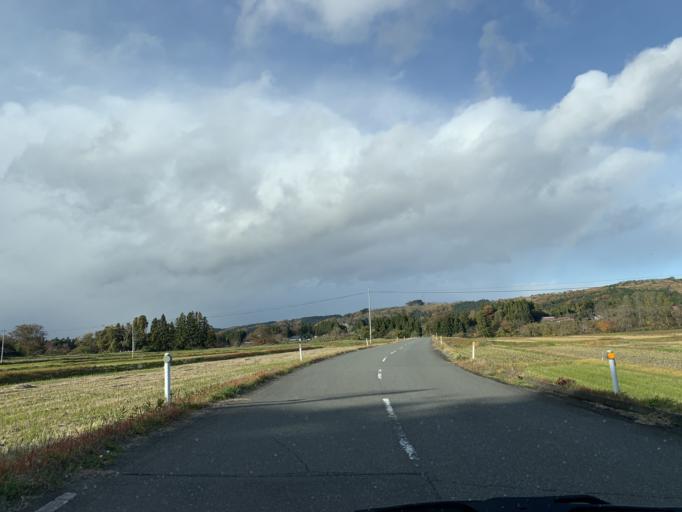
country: JP
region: Iwate
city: Ichinoseki
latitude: 39.0242
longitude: 141.0733
